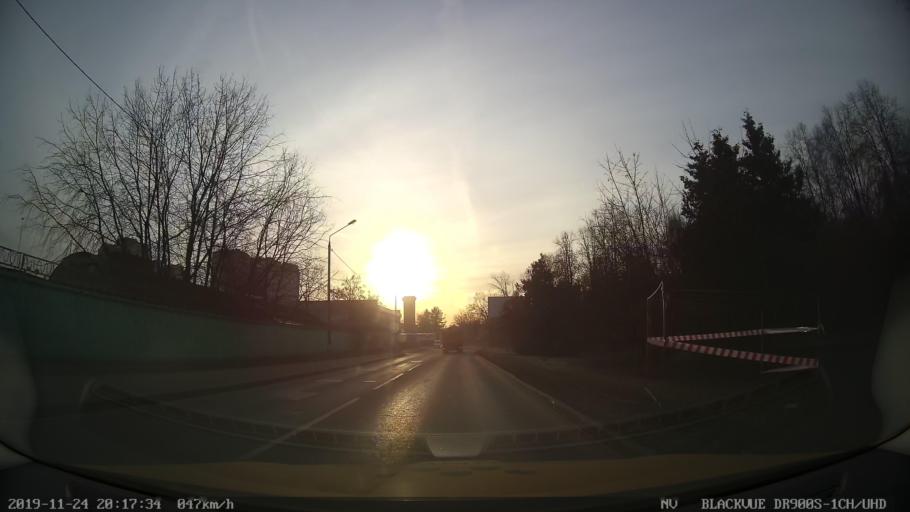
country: RU
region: Moskovskaya
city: Korolev
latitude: 55.9145
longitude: 37.8370
